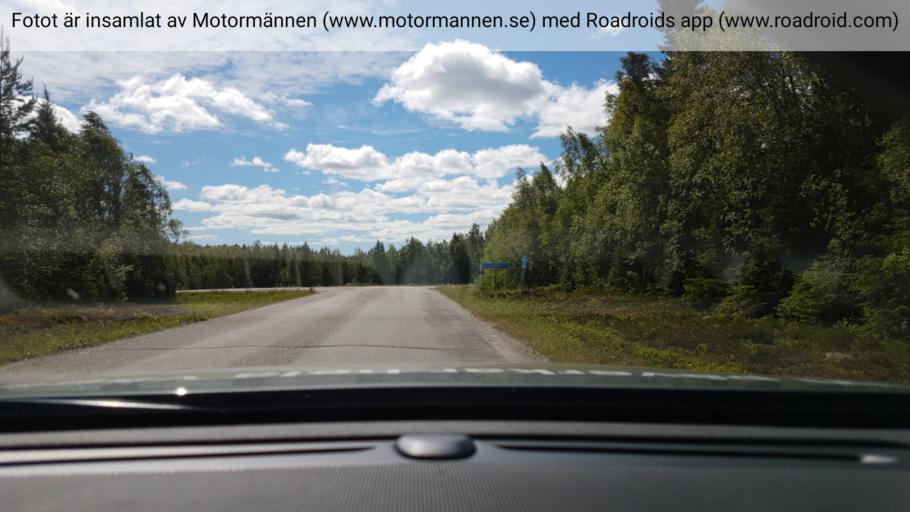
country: SE
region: Vaesterbotten
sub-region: Skelleftea Kommun
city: Burea
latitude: 64.4116
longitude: 21.3503
